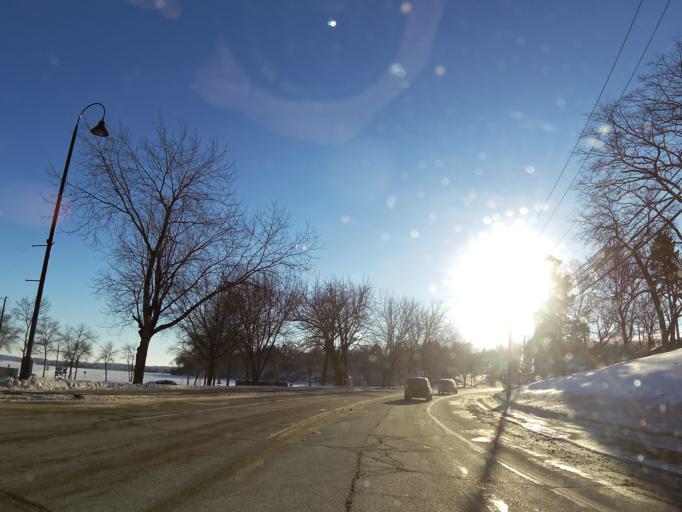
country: US
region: Minnesota
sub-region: Hennepin County
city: Mound
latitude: 44.9302
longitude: -93.6696
